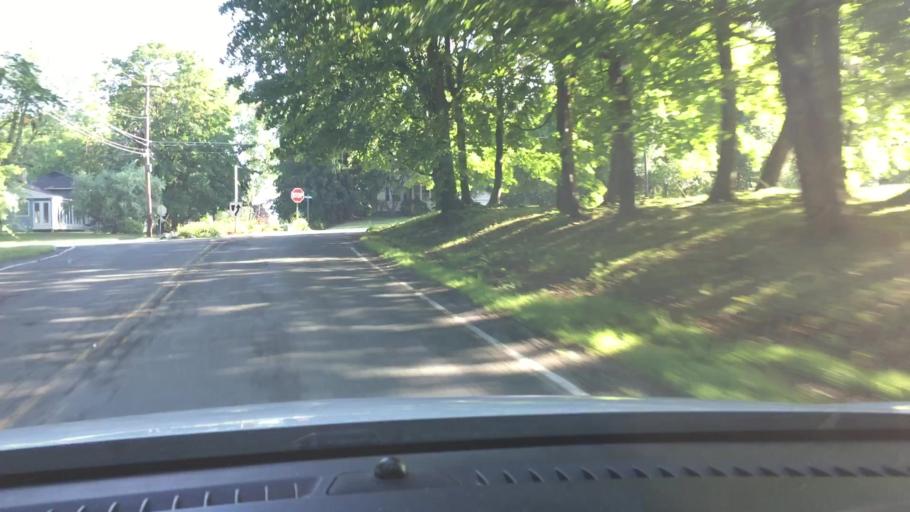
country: US
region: Massachusetts
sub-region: Berkshire County
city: Pittsfield
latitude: 42.4337
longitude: -73.2257
